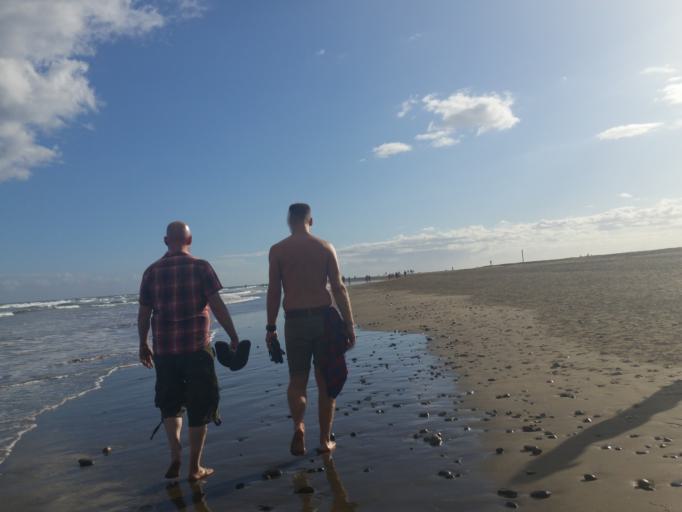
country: ES
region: Canary Islands
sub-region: Provincia de Las Palmas
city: Playa del Ingles
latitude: 27.7415
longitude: -15.5685
